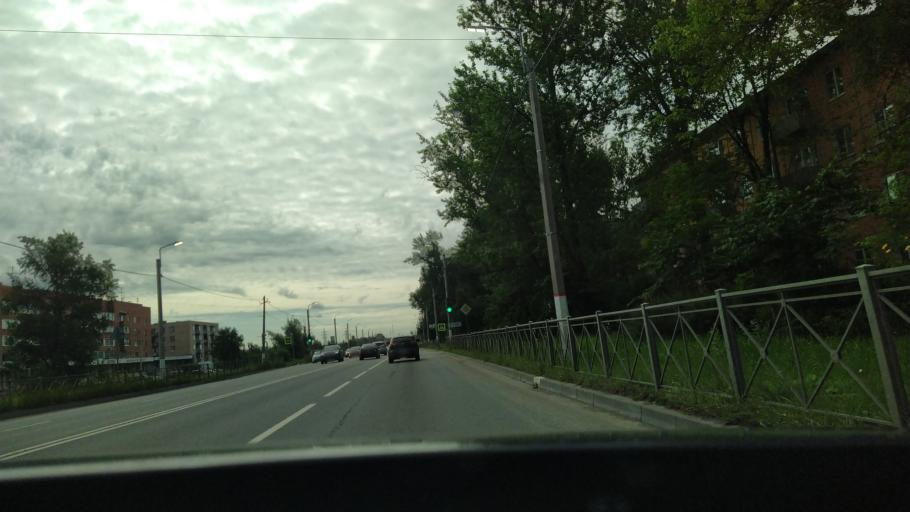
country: RU
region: Leningrad
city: Tosno
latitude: 59.5583
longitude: 30.8452
